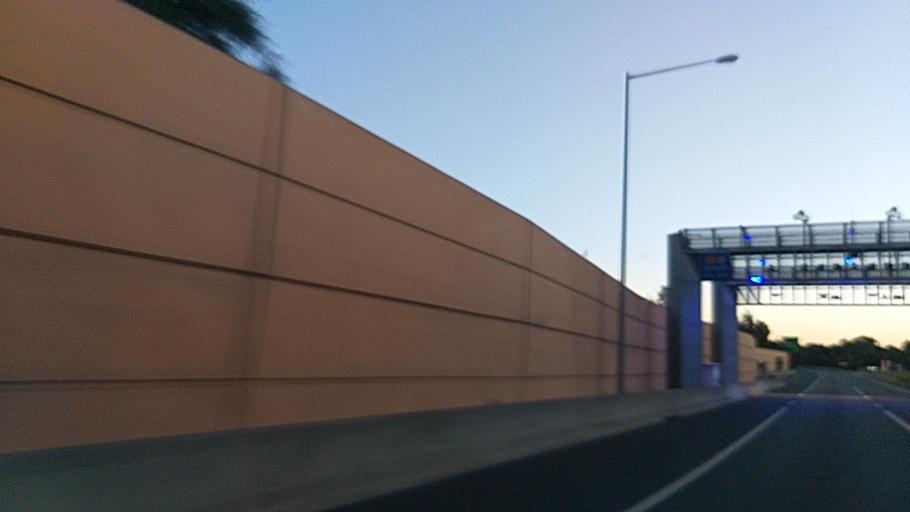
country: AU
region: New South Wales
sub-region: Liverpool
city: Miller
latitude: -33.9435
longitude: 150.8780
